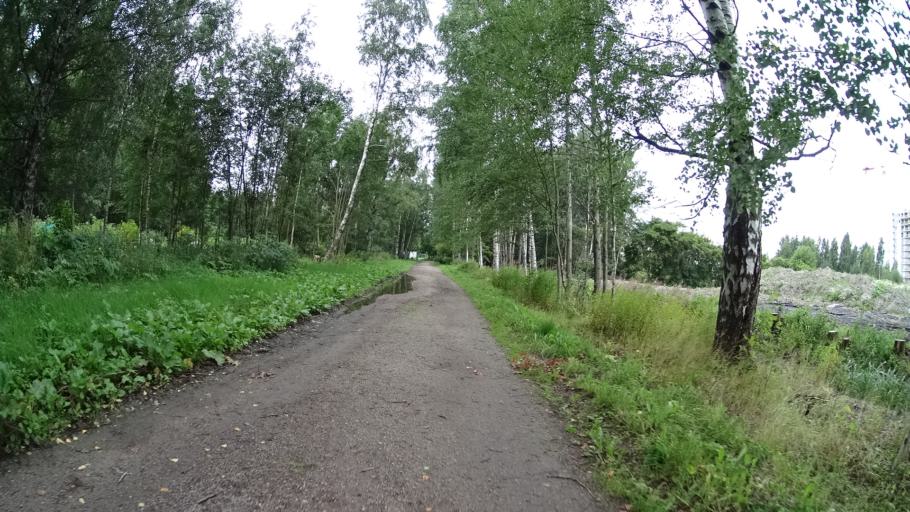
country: FI
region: Uusimaa
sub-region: Helsinki
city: Teekkarikylae
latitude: 60.2121
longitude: 24.8288
